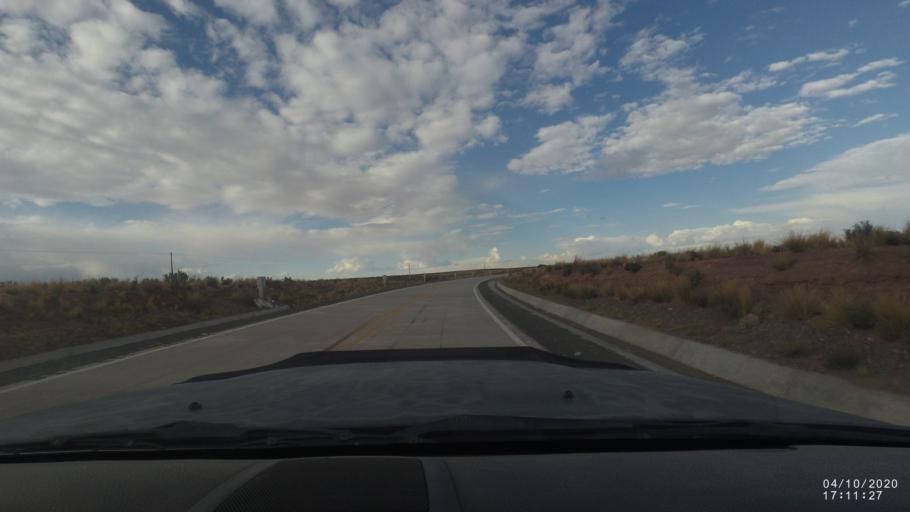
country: BO
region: Oruro
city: Oruro
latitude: -18.3197
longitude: -67.5764
